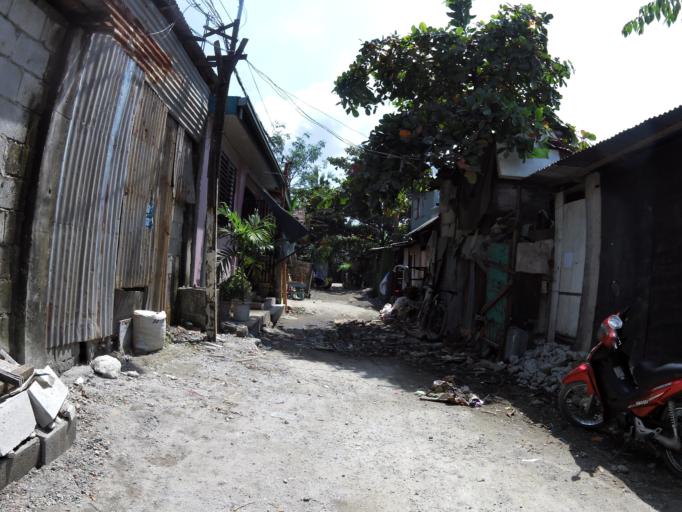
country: PH
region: Calabarzon
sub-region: Province of Rizal
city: Taguig
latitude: 14.5355
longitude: 121.1061
